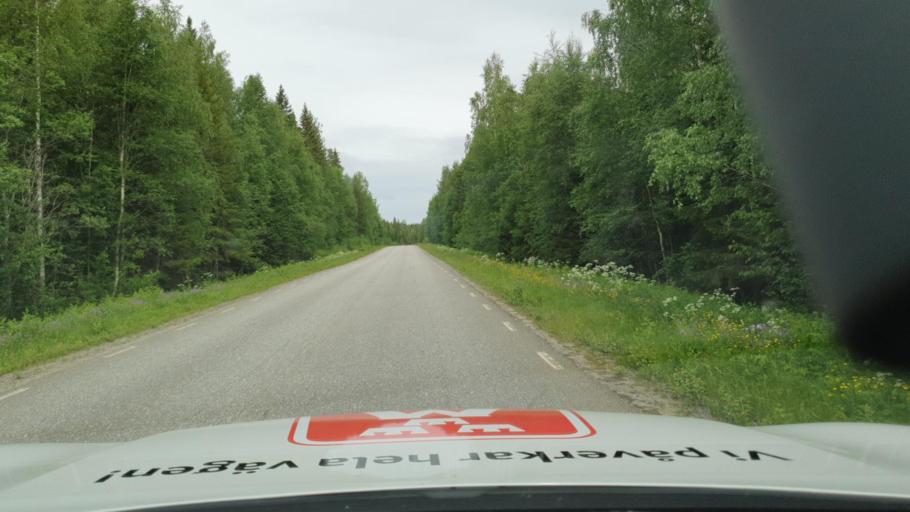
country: SE
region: Vaesterbotten
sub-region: Robertsfors Kommun
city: Robertsfors
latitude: 64.2911
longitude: 20.6474
